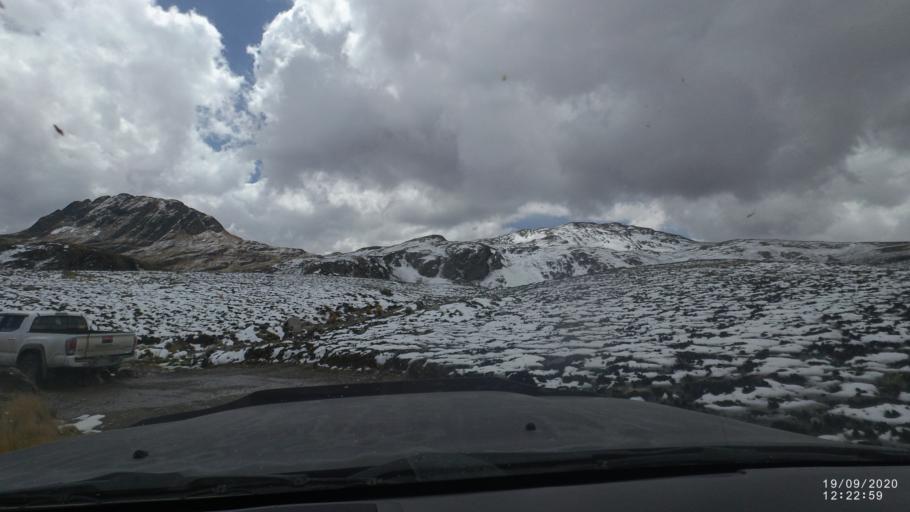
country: BO
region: Cochabamba
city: Cochabamba
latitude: -17.2958
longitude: -66.1085
